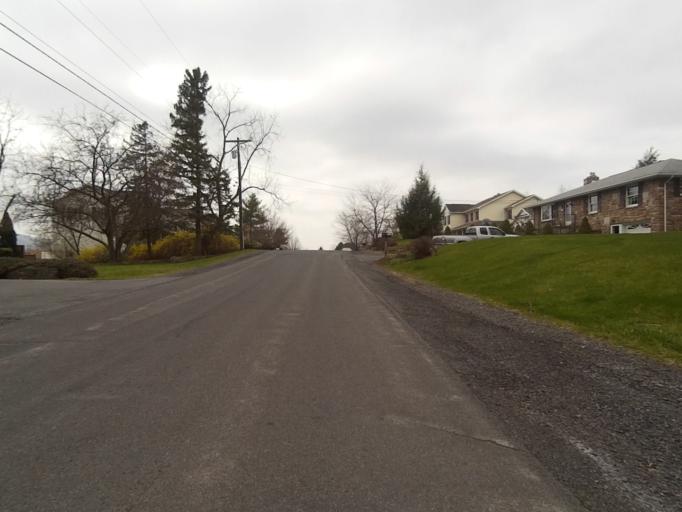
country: US
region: Pennsylvania
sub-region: Centre County
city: Boalsburg
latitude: 40.7848
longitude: -77.7770
